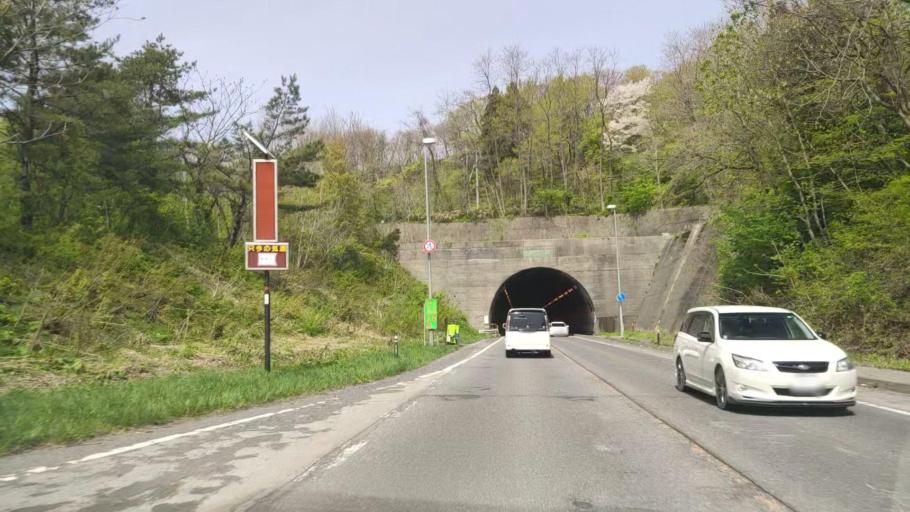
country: JP
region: Aomori
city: Aomori Shi
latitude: 40.8555
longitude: 140.8399
